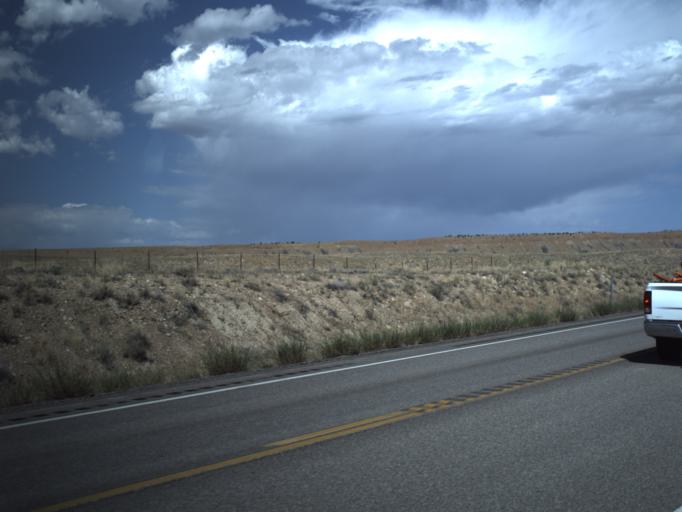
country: US
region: Utah
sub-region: Carbon County
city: East Carbon City
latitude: 39.3831
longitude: -110.4081
